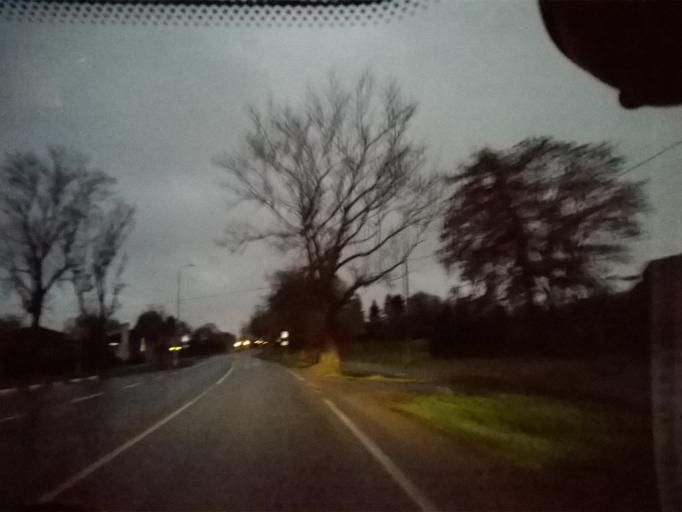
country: EE
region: Harju
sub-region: Viimsi vald
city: Viimsi
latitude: 59.5167
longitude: 24.8472
